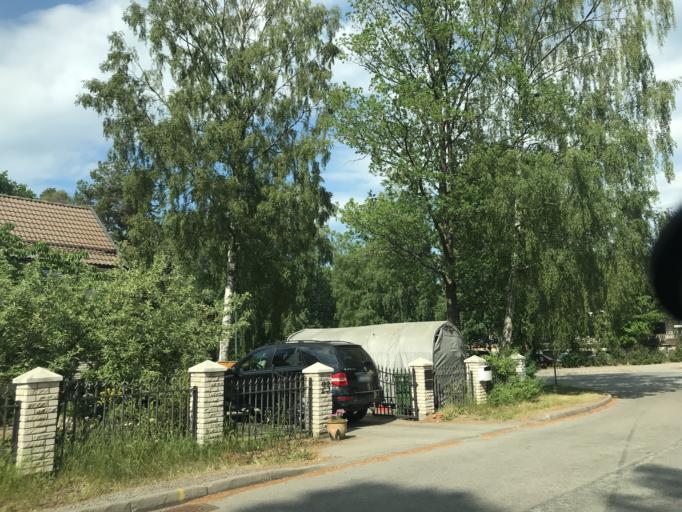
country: SE
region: Stockholm
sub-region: Stockholms Kommun
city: Kista
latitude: 59.4098
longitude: 17.9685
